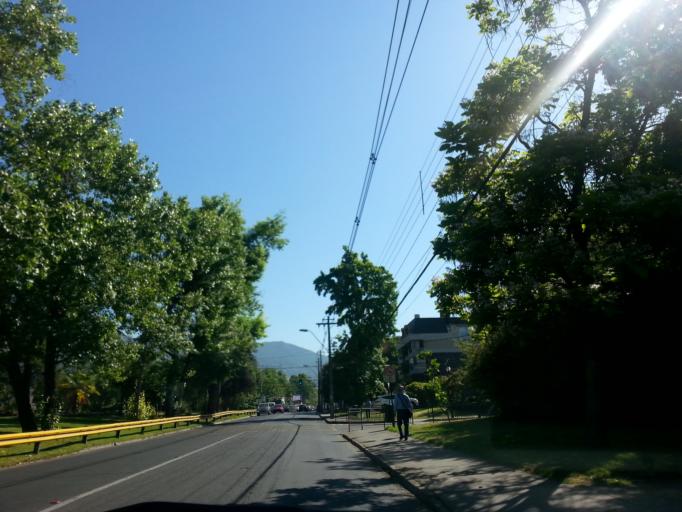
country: CL
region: Santiago Metropolitan
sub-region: Provincia de Santiago
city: Villa Presidente Frei, Nunoa, Santiago, Chile
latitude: -33.3873
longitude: -70.5932
